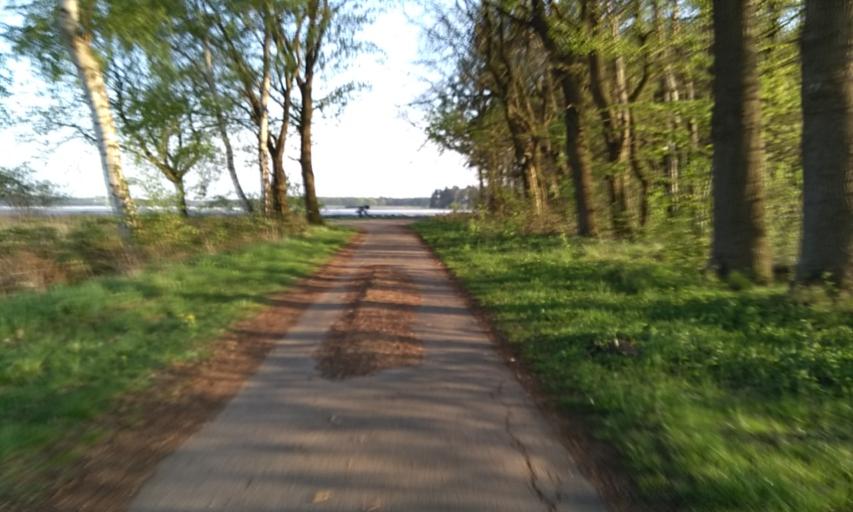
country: DE
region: Lower Saxony
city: Dollern
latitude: 53.5307
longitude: 9.5447
